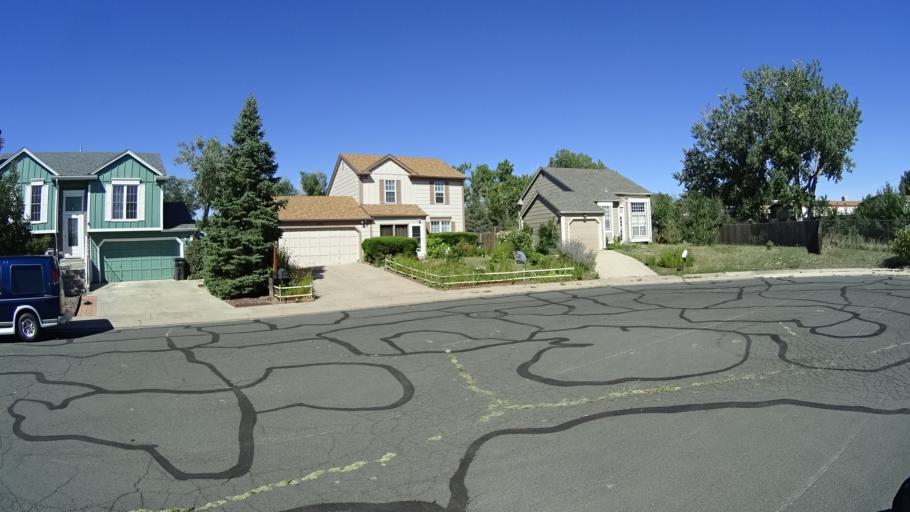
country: US
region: Colorado
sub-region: El Paso County
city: Stratmoor
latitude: 38.7956
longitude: -104.7351
